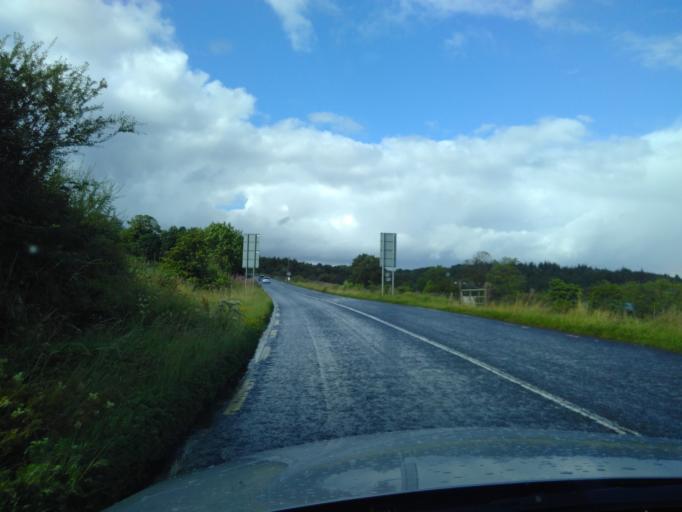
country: IE
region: Ulster
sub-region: County Donegal
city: Letterkenny
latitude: 54.9667
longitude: -7.6904
